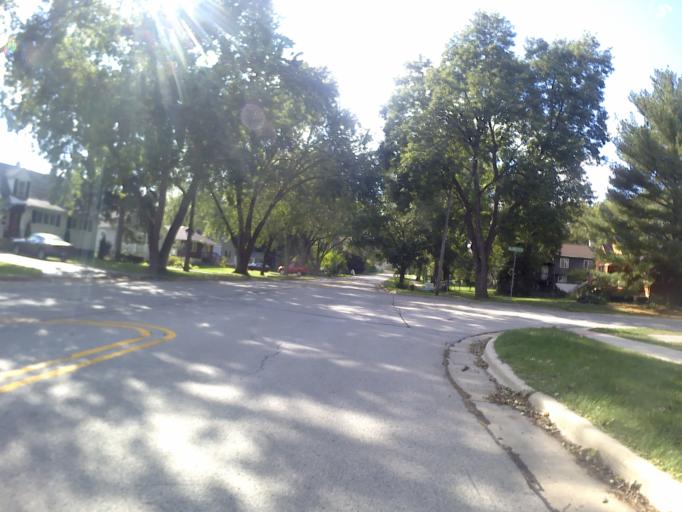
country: US
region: Illinois
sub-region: DuPage County
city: Lisle
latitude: 41.7976
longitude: -88.0786
